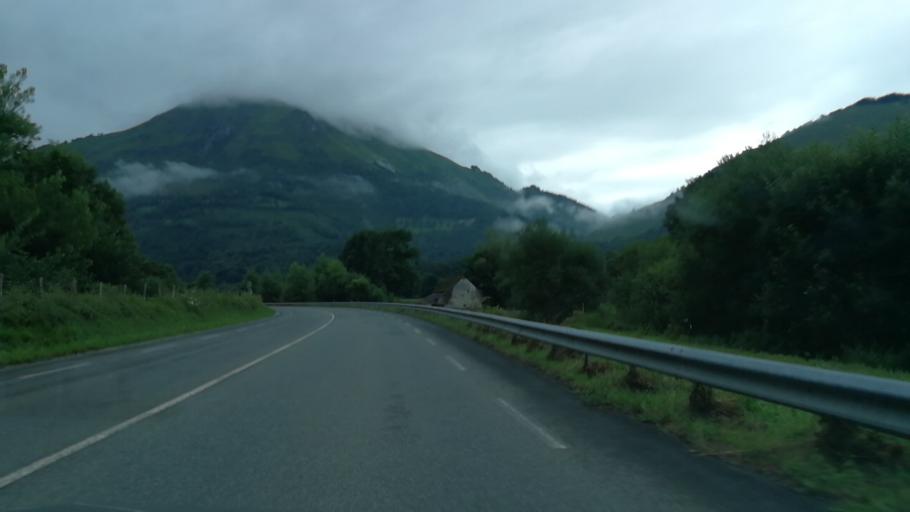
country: FR
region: Aquitaine
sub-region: Departement des Pyrenees-Atlantiques
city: Arette
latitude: 42.9872
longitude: -0.6105
